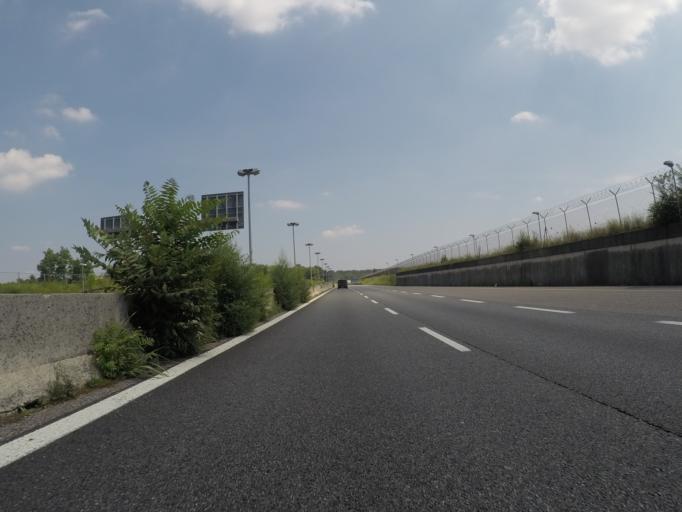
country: IT
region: Lombardy
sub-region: Provincia di Varese
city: Casorate Sempione
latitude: 45.6533
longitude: 8.7254
